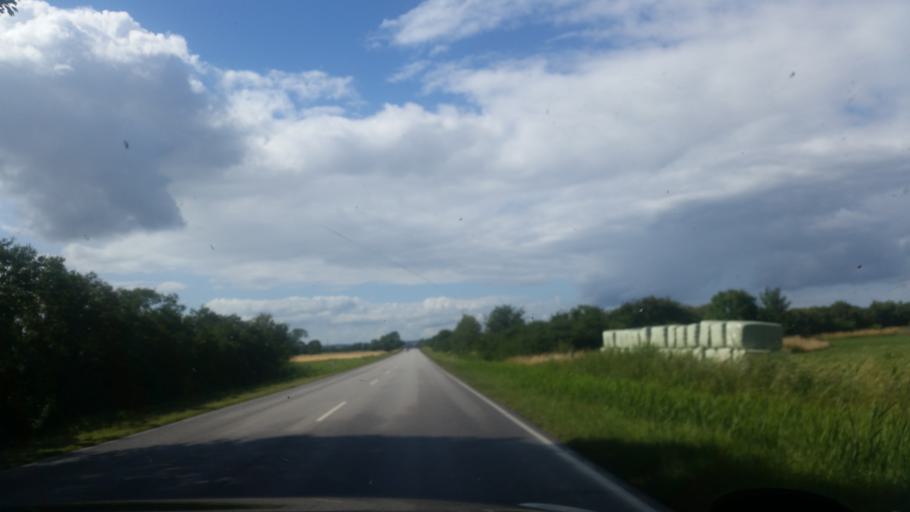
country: DK
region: Zealand
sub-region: Holbaek Kommune
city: Svinninge
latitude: 55.7482
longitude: 11.5277
